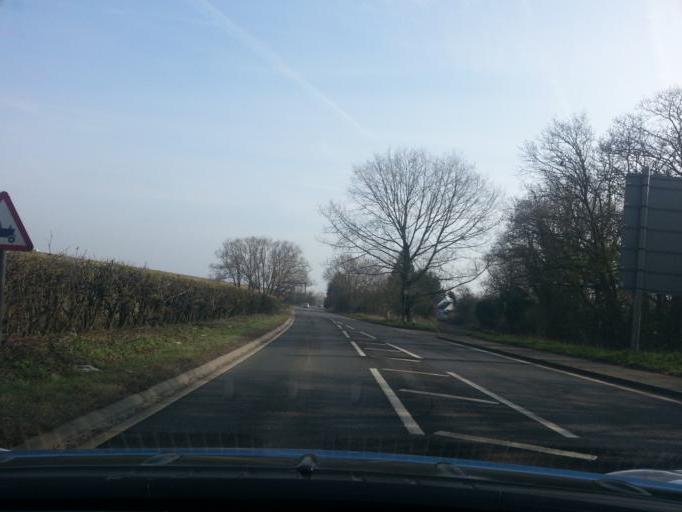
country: GB
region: England
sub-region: Borough of Swindon
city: Wanborough
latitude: 51.5832
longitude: -1.7055
